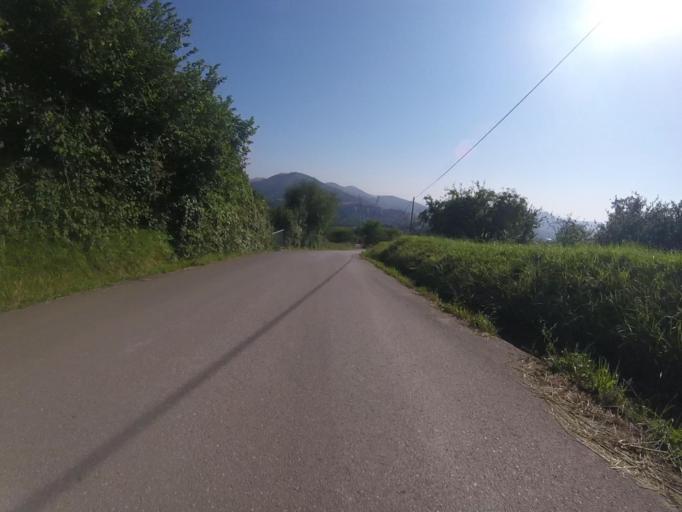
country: ES
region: Basque Country
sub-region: Provincia de Guipuzcoa
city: Astigarraga
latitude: 43.2648
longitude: -1.9361
